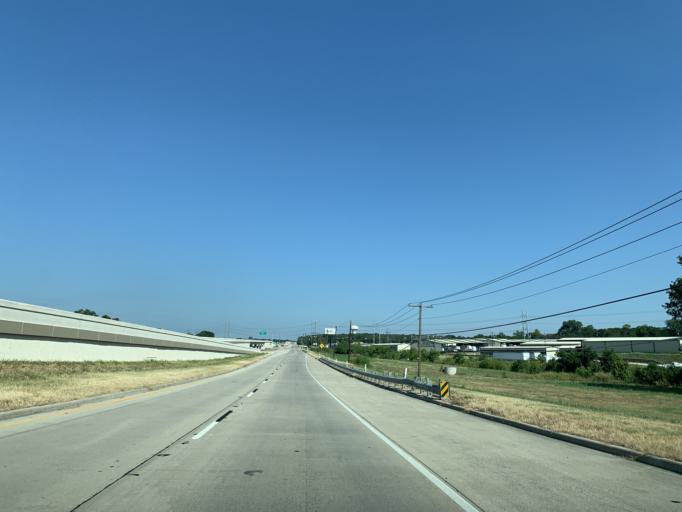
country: US
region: Texas
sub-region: Tarrant County
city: Lakeside
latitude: 32.8532
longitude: -97.5079
